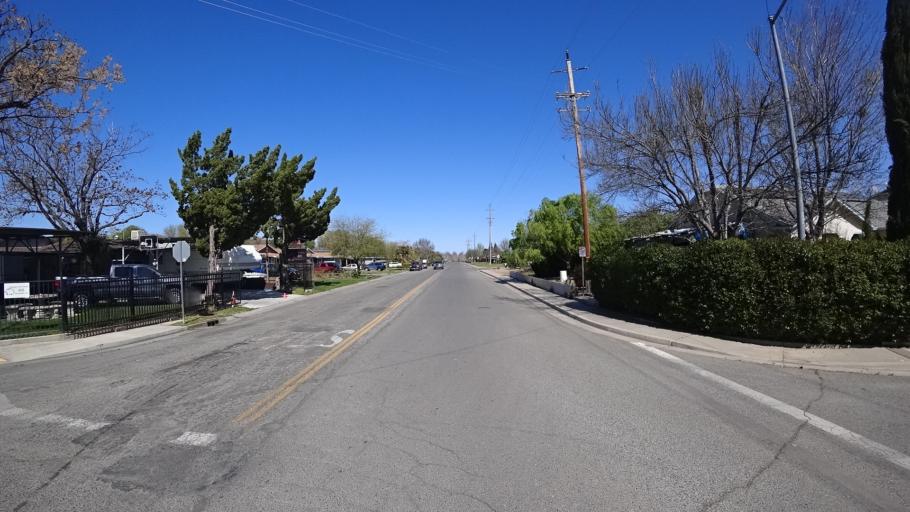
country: US
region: California
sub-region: Glenn County
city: Hamilton City
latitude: 39.7445
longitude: -122.0079
